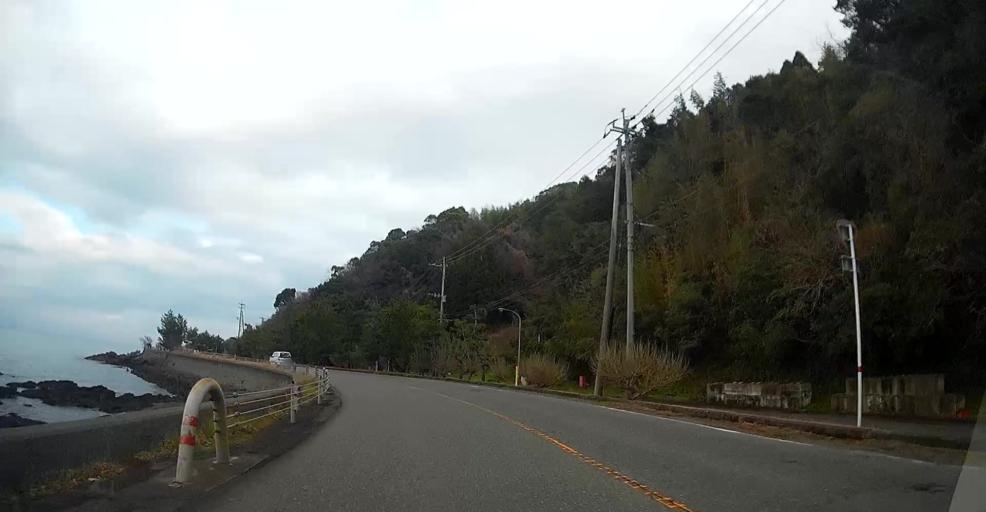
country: JP
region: Kumamoto
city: Hondo
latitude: 32.4887
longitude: 130.2900
